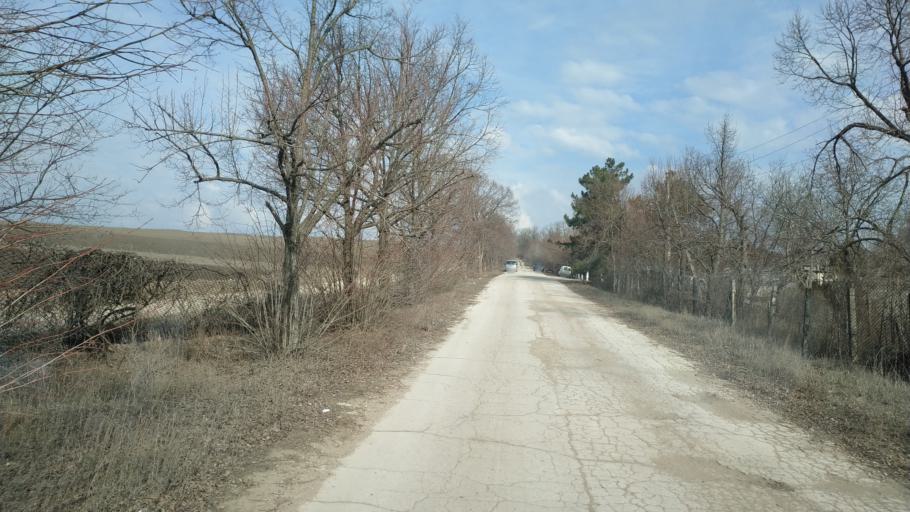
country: MD
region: Anenii Noi
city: Anenii Noi
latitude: 46.9427
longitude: 29.1104
